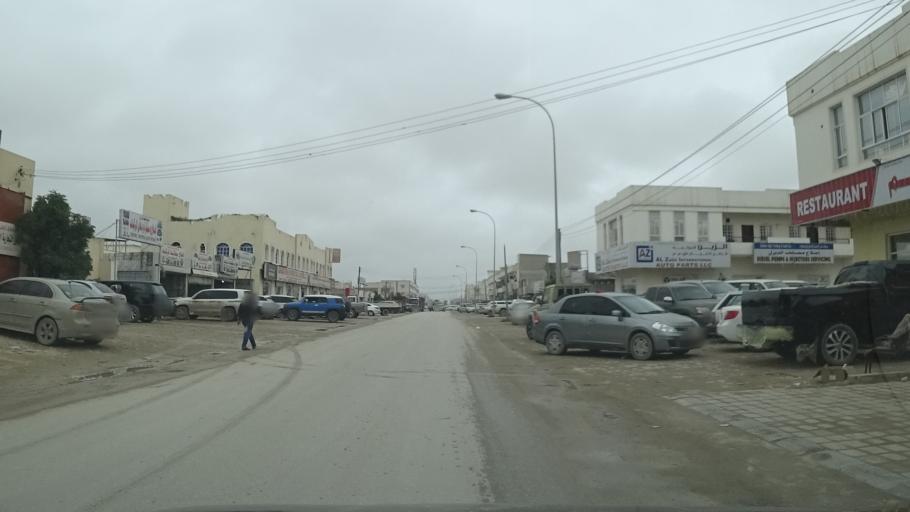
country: OM
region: Zufar
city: Salalah
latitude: 17.0197
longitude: 54.0499
